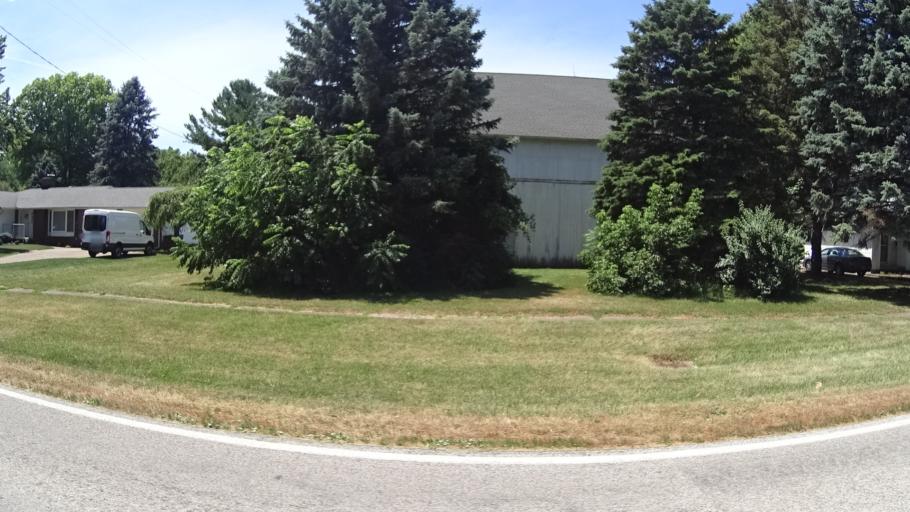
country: US
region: Ohio
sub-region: Erie County
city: Sandusky
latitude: 41.3901
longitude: -82.6706
